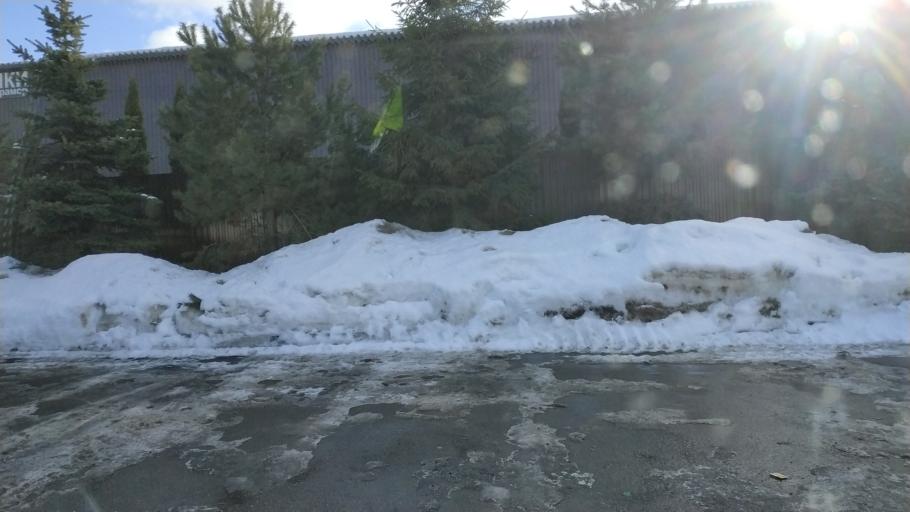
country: RU
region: Moskovskaya
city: Mosrentgen
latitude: 55.6074
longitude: 37.4517
